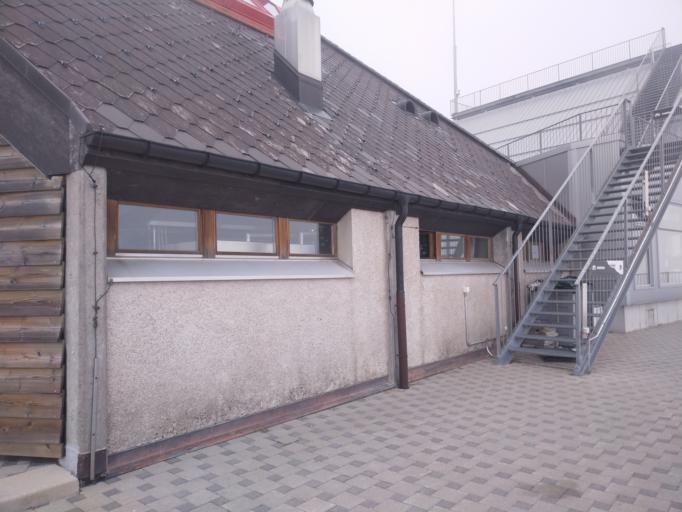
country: CH
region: Fribourg
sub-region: Gruyere District
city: Vuadens
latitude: 46.5469
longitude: 7.0182
